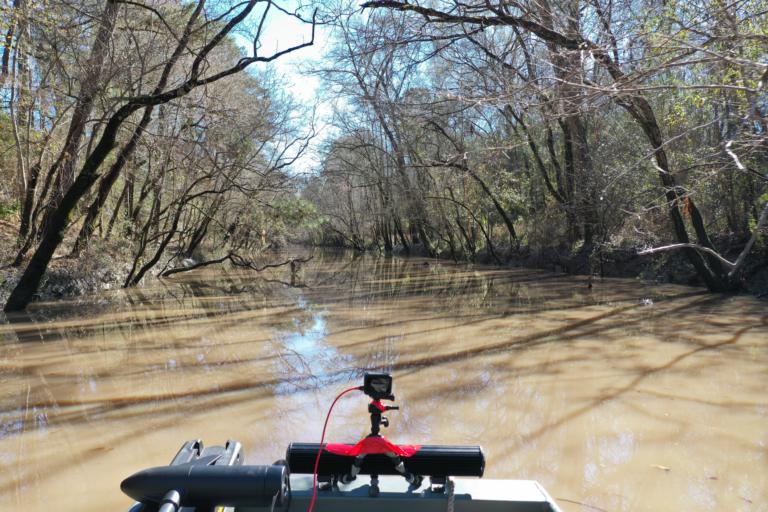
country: US
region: Louisiana
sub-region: Calcasieu Parish
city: Iowa
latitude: 30.3157
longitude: -93.0473
